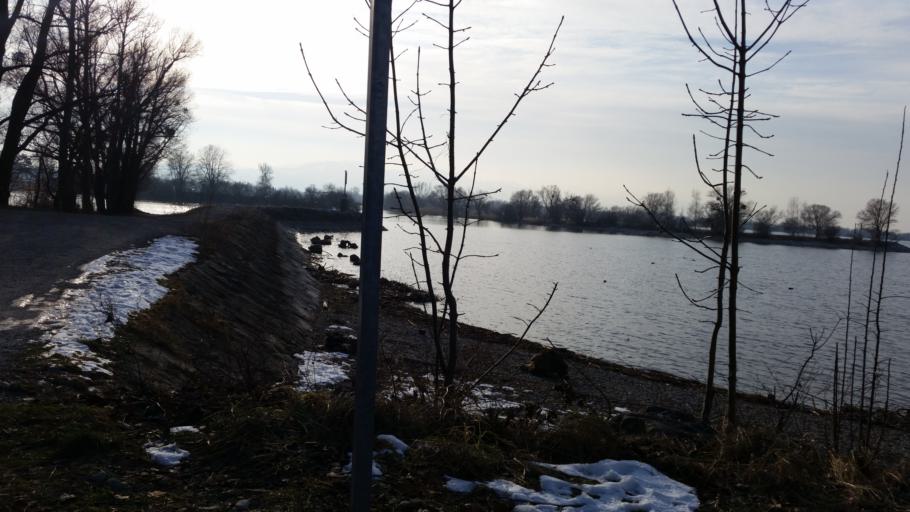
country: AT
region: Vorarlberg
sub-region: Politischer Bezirk Bregenz
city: Hard
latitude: 47.5022
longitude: 9.6879
